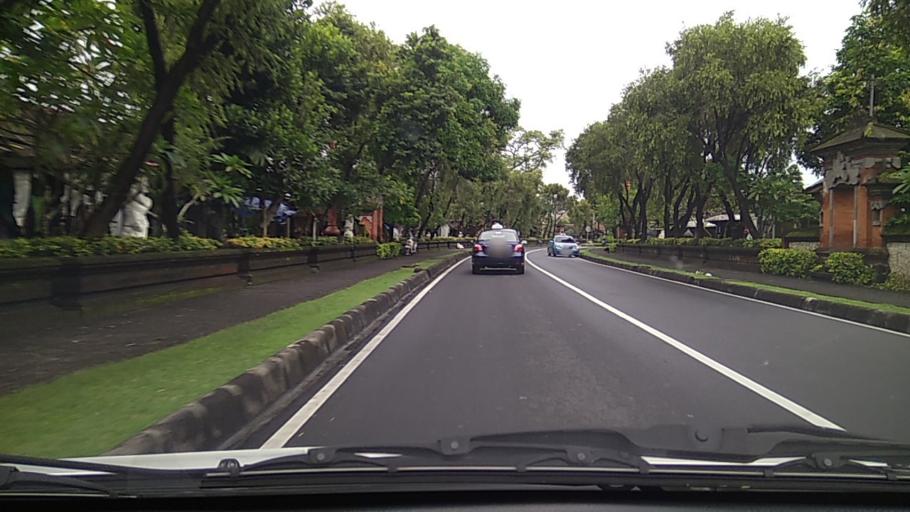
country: ID
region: Bali
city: Bualu
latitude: -8.7981
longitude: 115.2248
